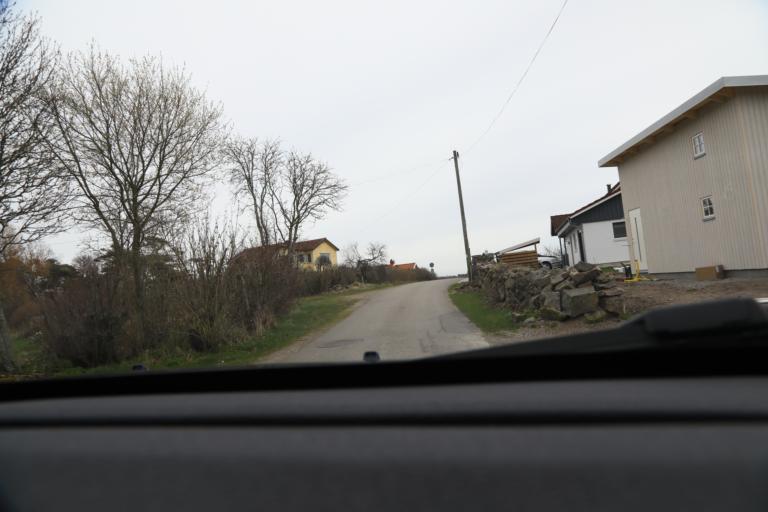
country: SE
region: Halland
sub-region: Varbergs Kommun
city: Traslovslage
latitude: 57.0734
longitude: 12.2688
